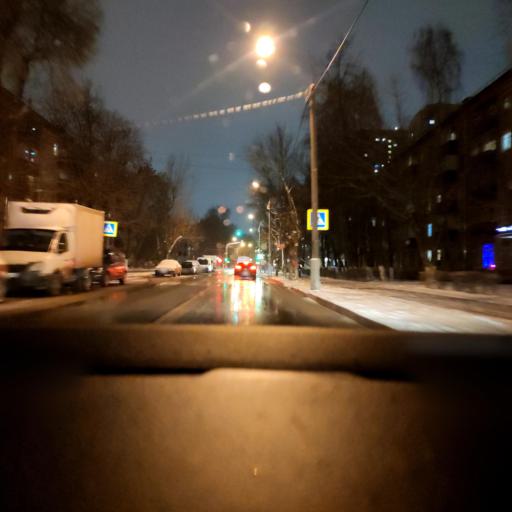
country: RU
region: Moskovskaya
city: Reutov
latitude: 55.7632
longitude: 37.8632
